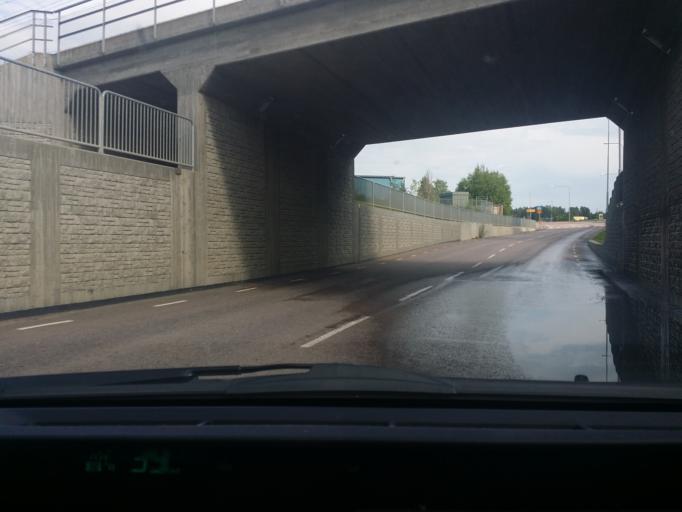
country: SE
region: Vaestmanland
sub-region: Hallstahammars Kommun
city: Kolback
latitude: 59.5656
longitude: 16.2374
